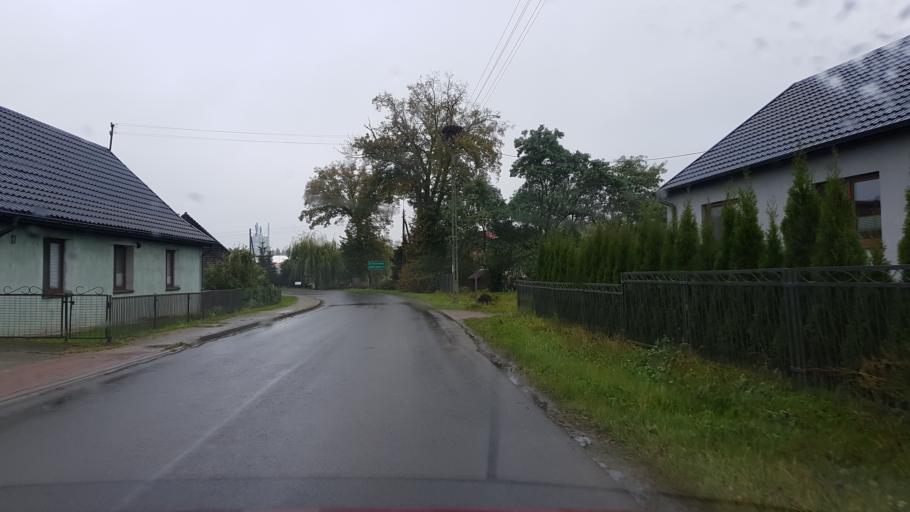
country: PL
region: Greater Poland Voivodeship
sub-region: Powiat zlotowski
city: Tarnowka
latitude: 53.3497
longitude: 16.9060
